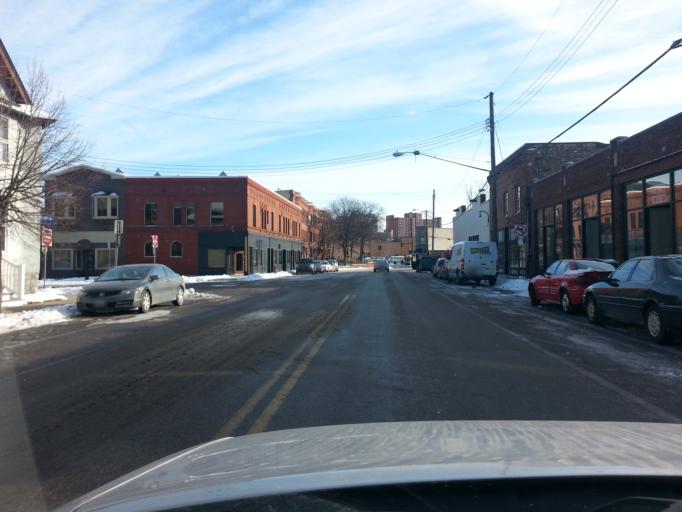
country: US
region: Minnesota
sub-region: Hennepin County
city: Minneapolis
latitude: 44.9695
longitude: -93.2642
